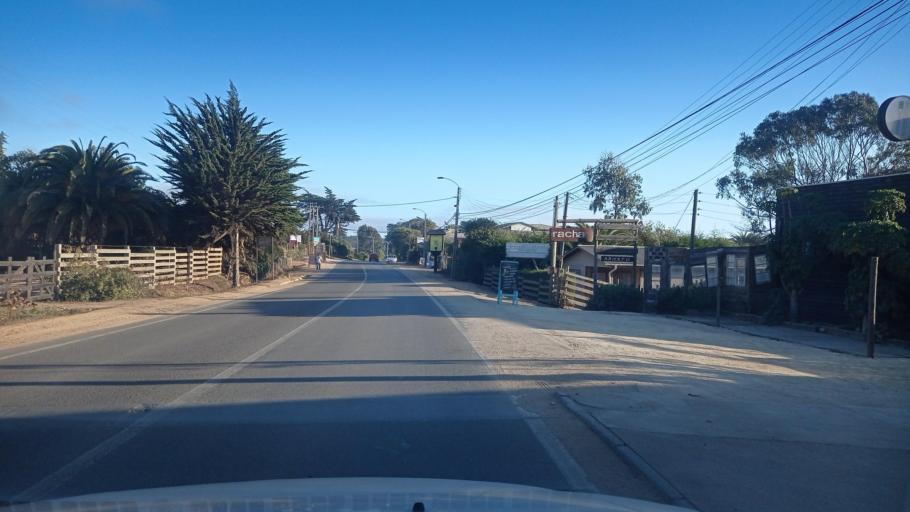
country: CL
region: O'Higgins
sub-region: Provincia de Colchagua
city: Santa Cruz
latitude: -34.4102
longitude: -72.0271
